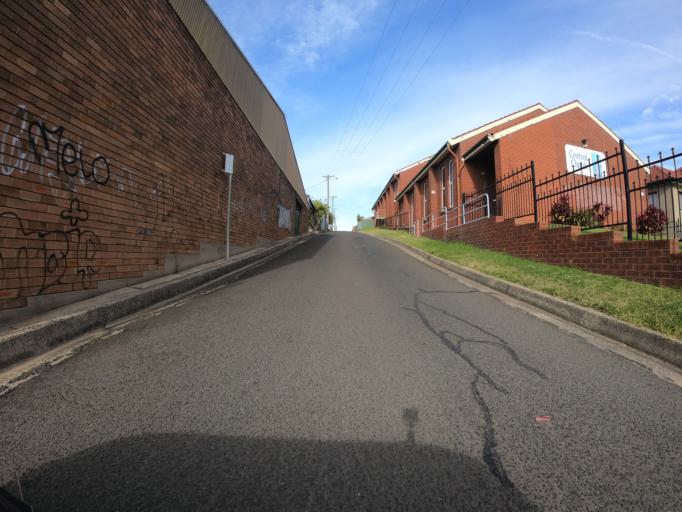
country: AU
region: New South Wales
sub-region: Wollongong
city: Port Kembla
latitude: -34.4832
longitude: 150.9029
